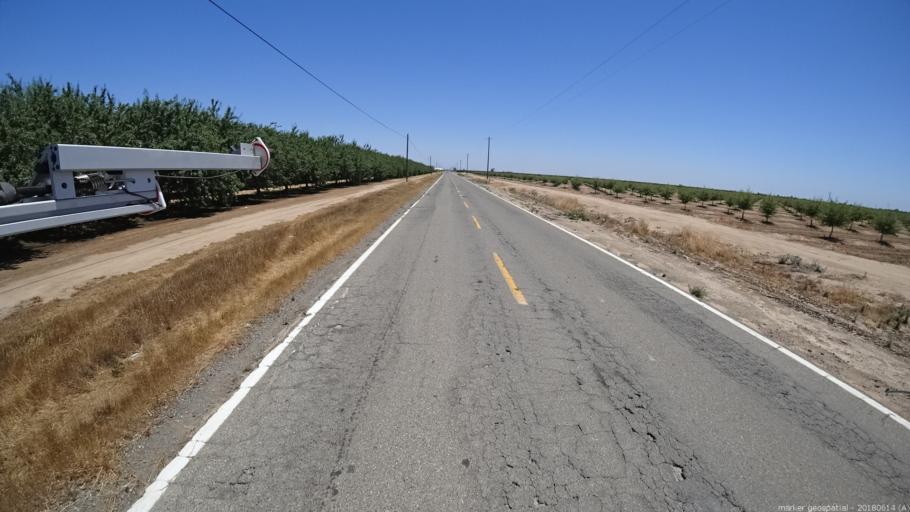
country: US
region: California
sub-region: Madera County
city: Fairmead
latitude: 37.0401
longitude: -120.1784
